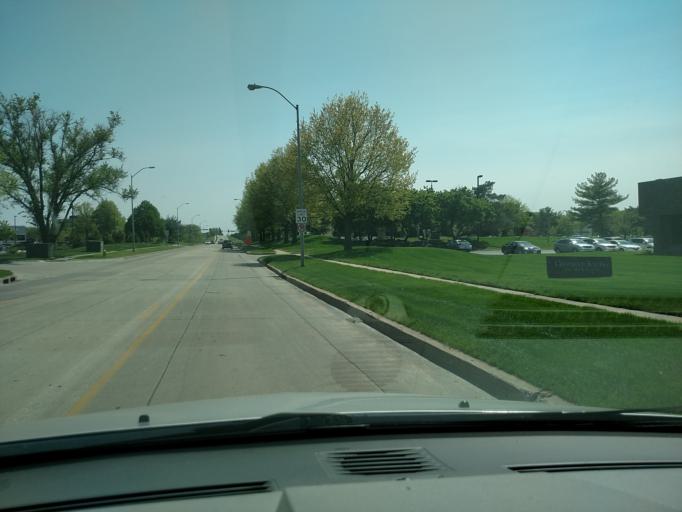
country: US
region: Iowa
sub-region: Polk County
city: Clive
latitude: 41.5979
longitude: -93.7617
